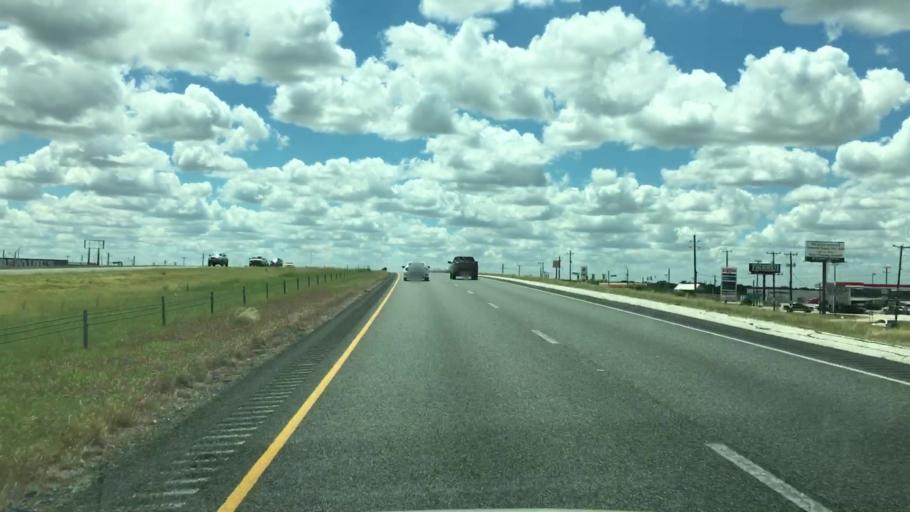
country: US
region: Texas
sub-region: Bexar County
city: Elmendorf
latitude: 29.2202
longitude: -98.4117
